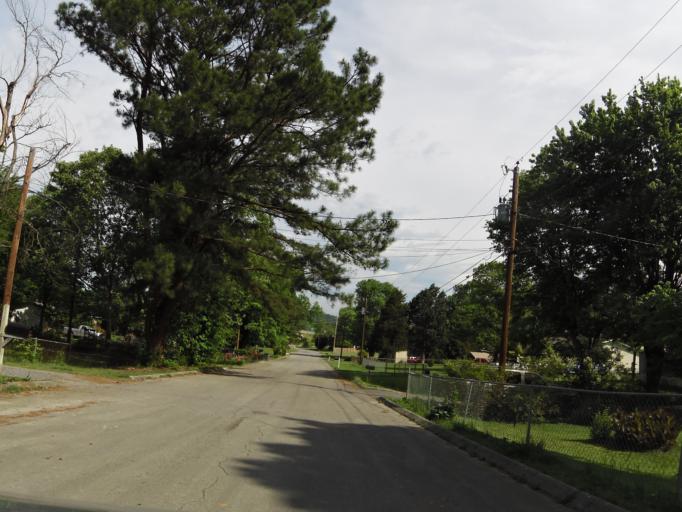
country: US
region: Tennessee
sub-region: Blount County
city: Alcoa
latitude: 35.8236
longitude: -83.9584
